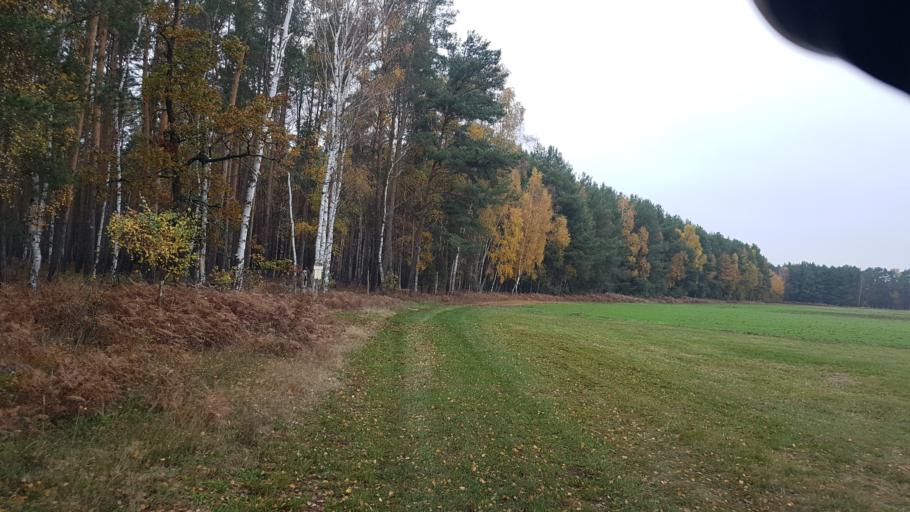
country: DE
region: Brandenburg
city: Ruckersdorf
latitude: 51.5729
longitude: 13.6441
